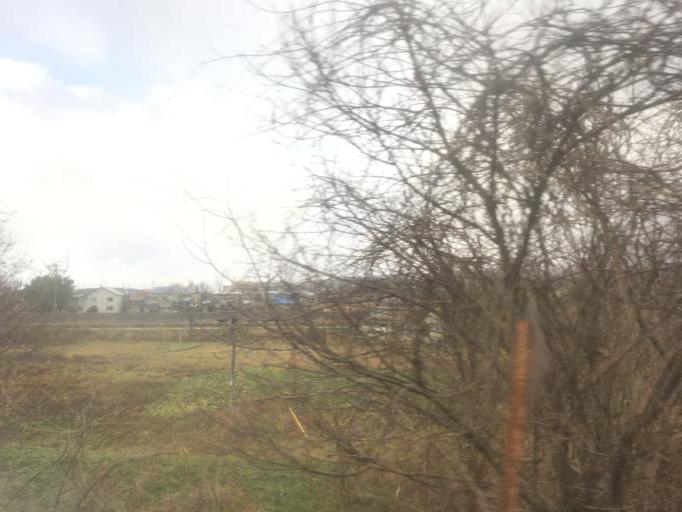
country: JP
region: Aomori
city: Goshogawara
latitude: 41.1816
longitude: 140.4884
